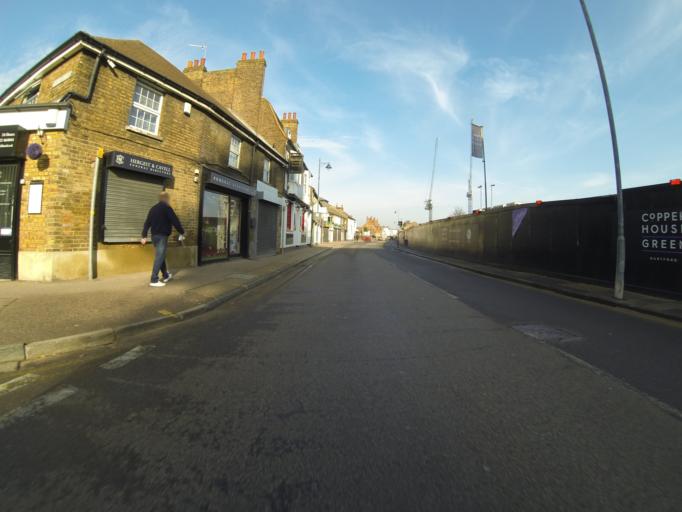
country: GB
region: England
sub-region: Kent
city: Dartford
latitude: 51.4412
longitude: 0.2155
